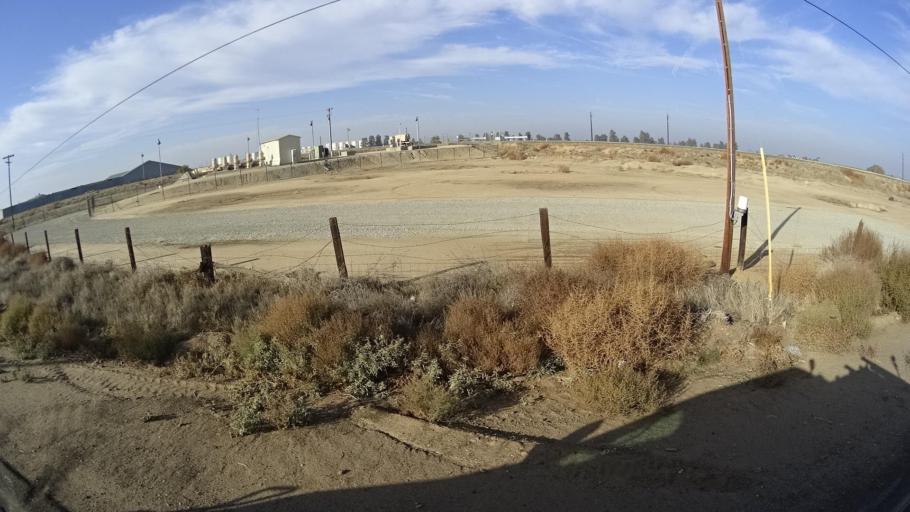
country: US
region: California
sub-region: Kern County
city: McFarland
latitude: 35.6373
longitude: -119.2045
